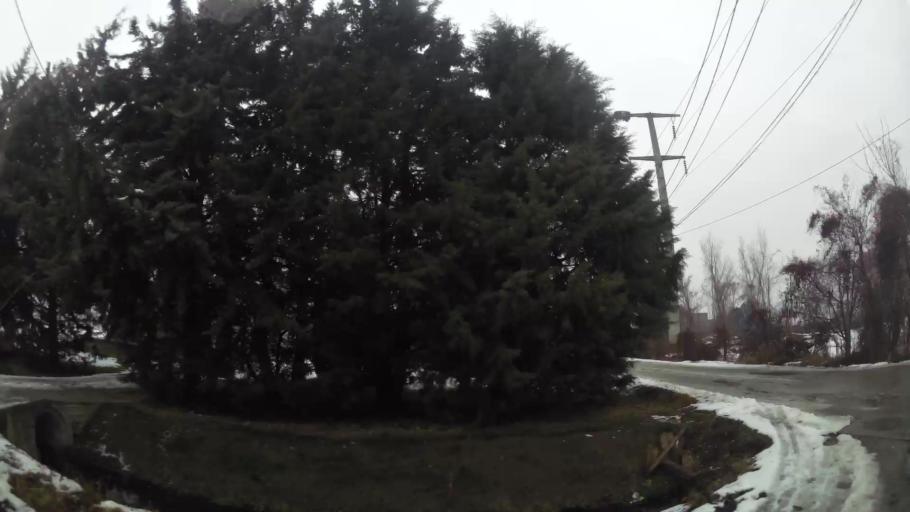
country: MK
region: Petrovec
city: Petrovec
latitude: 41.9367
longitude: 21.6100
